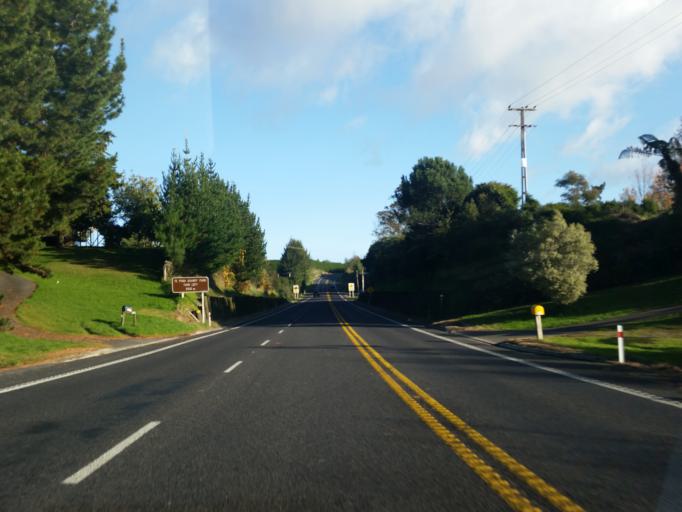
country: NZ
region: Bay of Plenty
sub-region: Tauranga City
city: Tauranga
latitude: -37.6976
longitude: 176.0557
